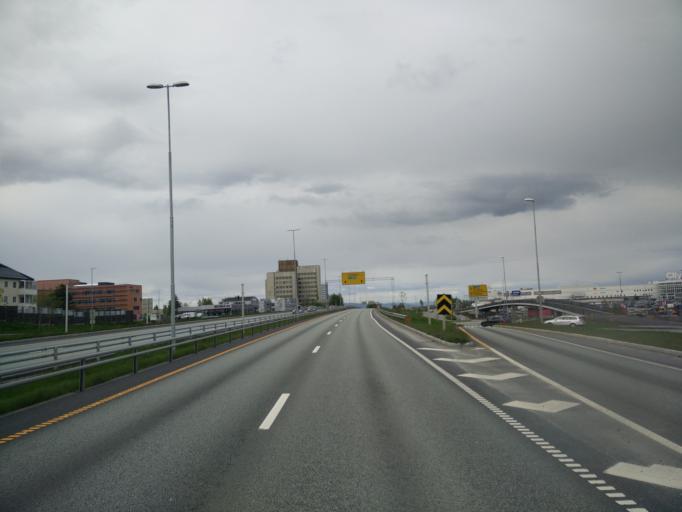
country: NO
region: Sor-Trondelag
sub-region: Trondheim
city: Trondheim
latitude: 63.3584
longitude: 10.3719
